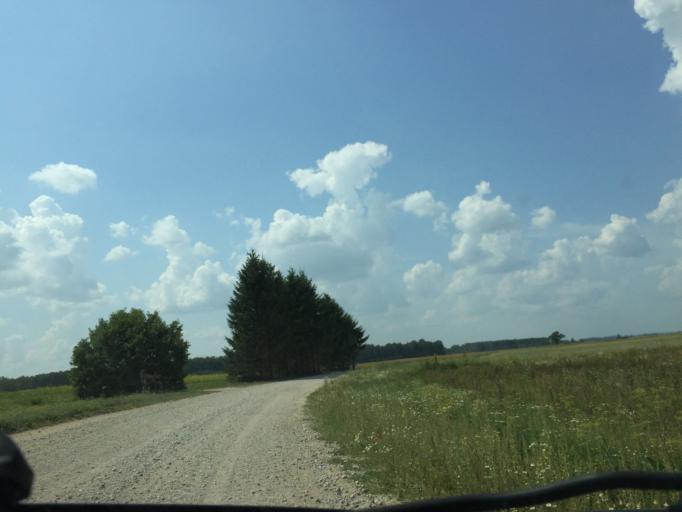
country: LT
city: Zagare
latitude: 56.3956
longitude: 23.2196
